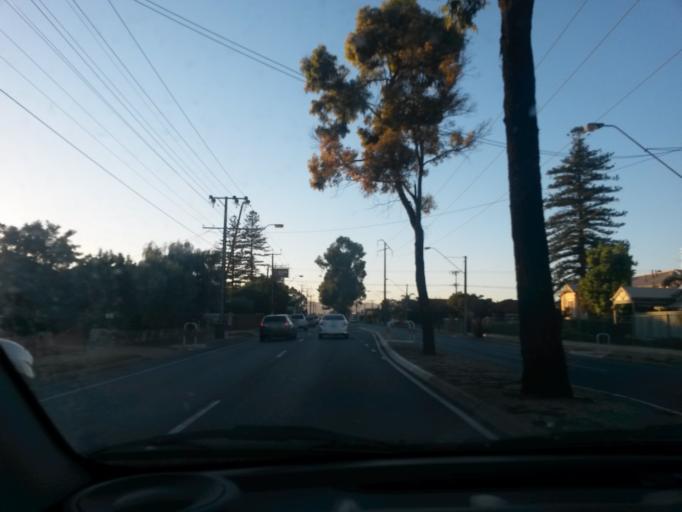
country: AU
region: South Australia
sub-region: Charles Sturt
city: Woodville North
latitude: -34.8736
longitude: 138.5458
